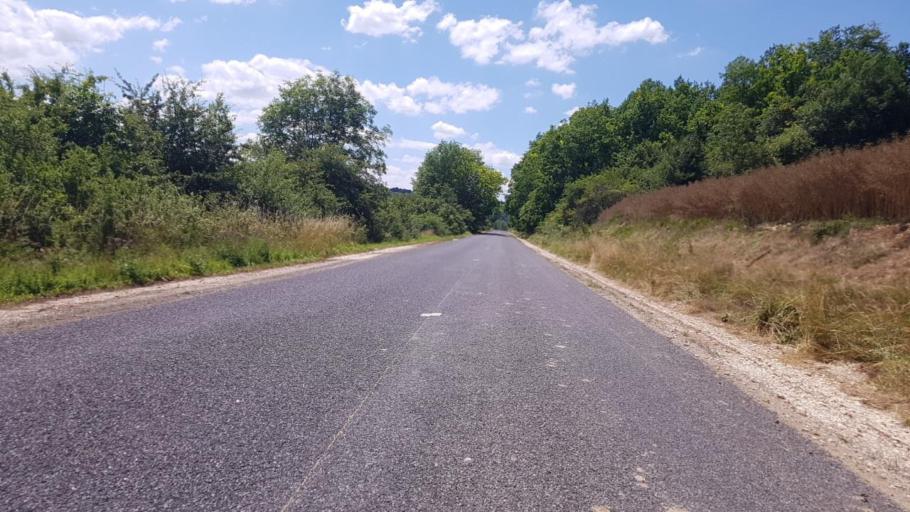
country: FR
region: Lorraine
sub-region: Departement de la Meuse
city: Ligny-en-Barrois
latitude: 48.6428
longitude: 5.3921
